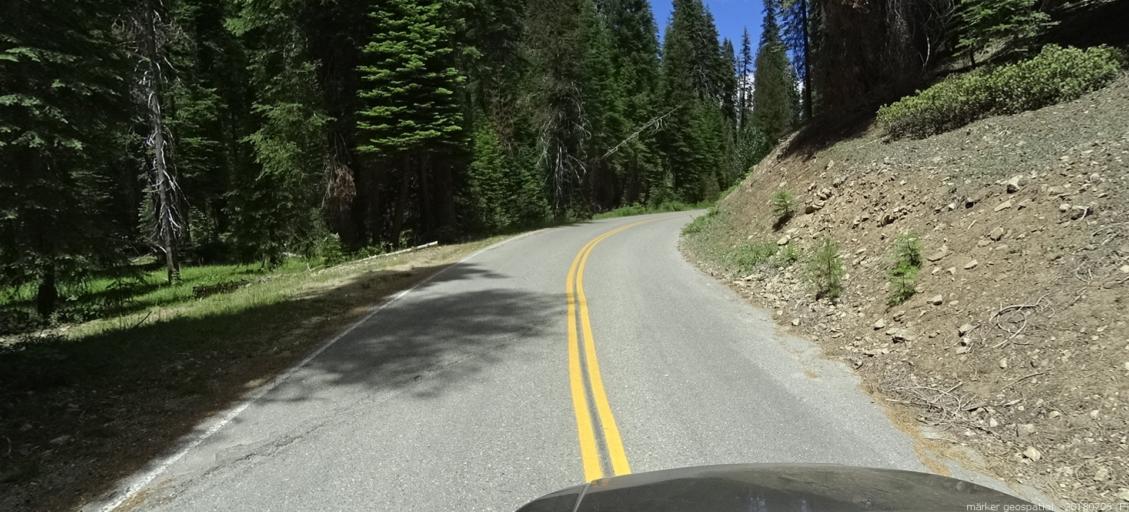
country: US
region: California
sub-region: Madera County
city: Oakhurst
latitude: 37.4285
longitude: -119.4307
